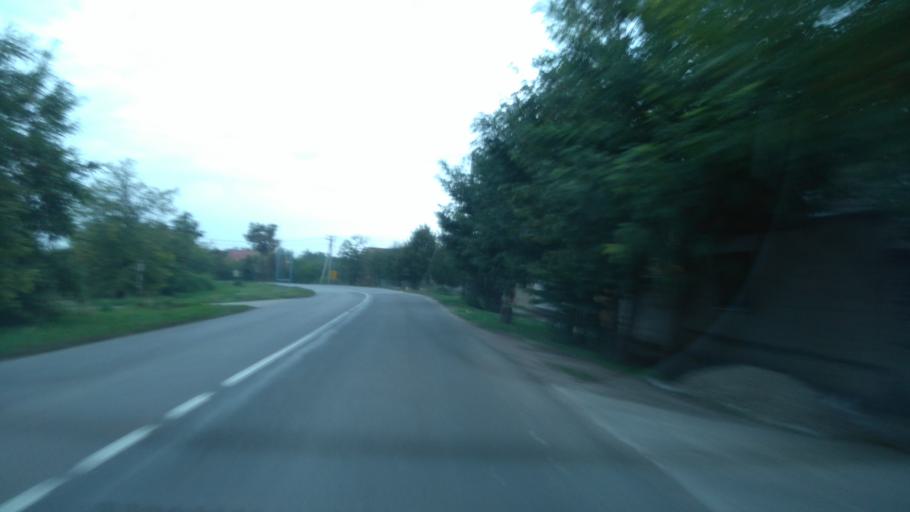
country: RS
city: Mol
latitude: 45.7784
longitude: 20.1354
